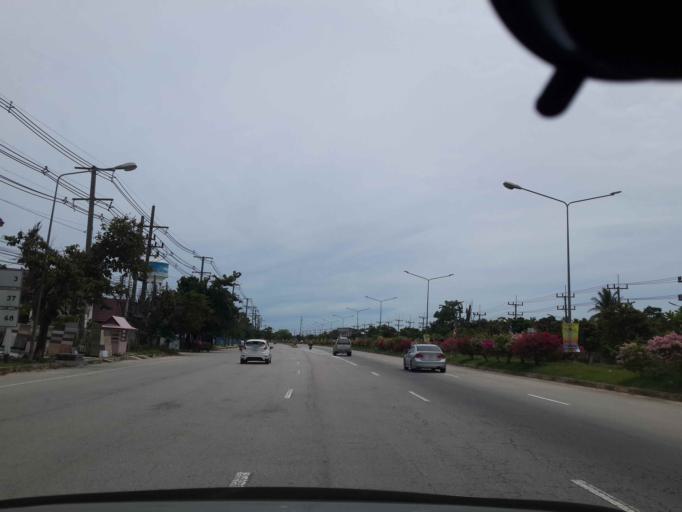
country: TH
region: Narathiwat
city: Narathiwat
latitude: 6.4108
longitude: 101.8033
